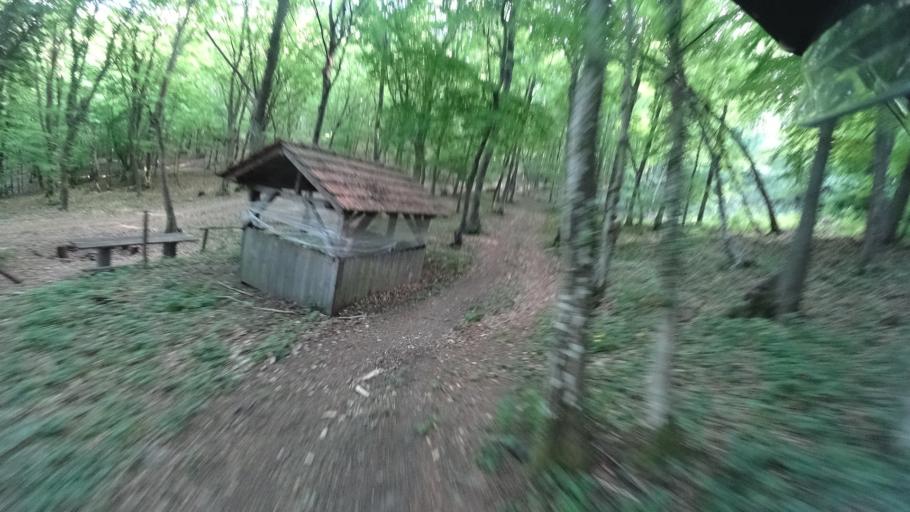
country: HR
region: Zagrebacka
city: Jablanovec
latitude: 45.8667
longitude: 15.8794
